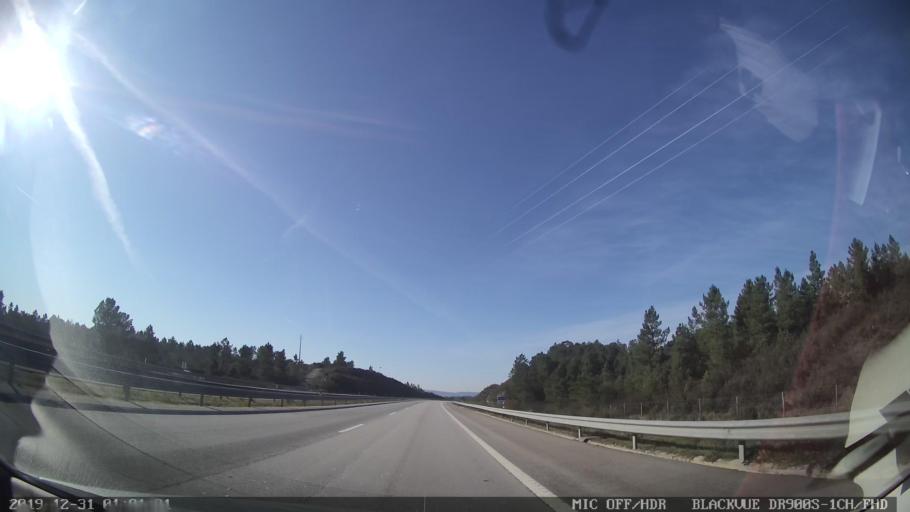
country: ES
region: Extremadura
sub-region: Provincia de Caceres
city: Cedillo
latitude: 39.7352
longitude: -7.6571
